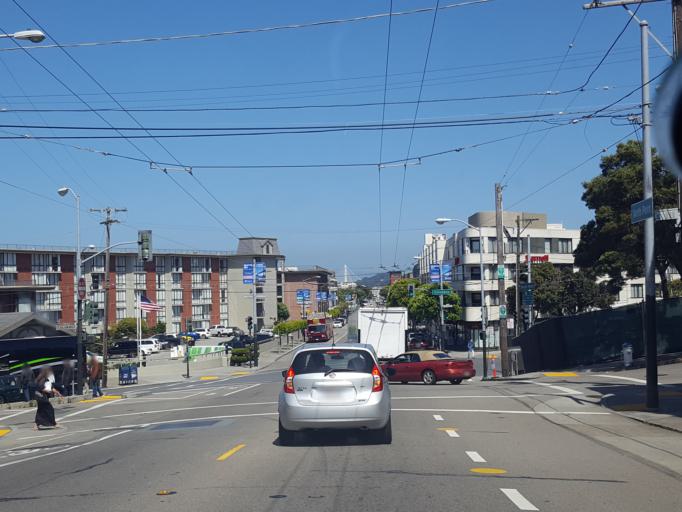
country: US
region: California
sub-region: San Francisco County
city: San Francisco
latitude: 37.8059
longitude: -122.4191
